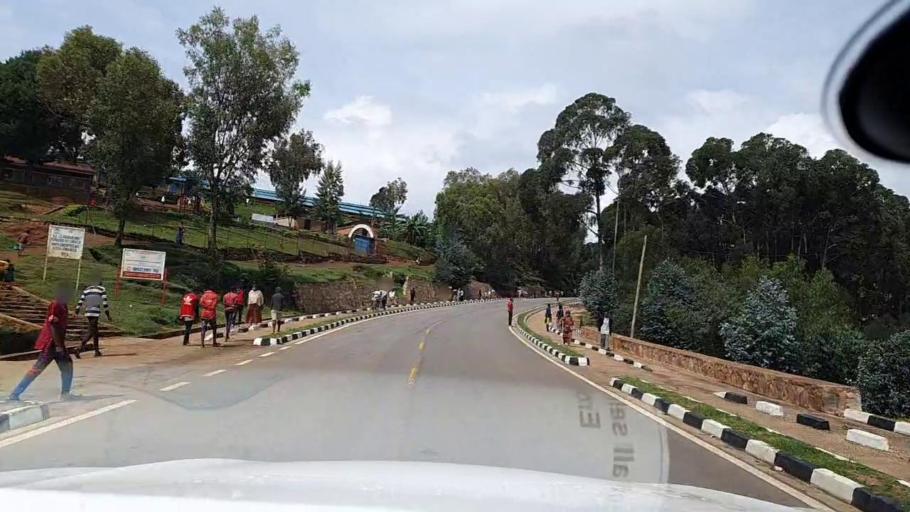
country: RW
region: Southern Province
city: Nzega
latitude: -2.4843
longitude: 29.5258
